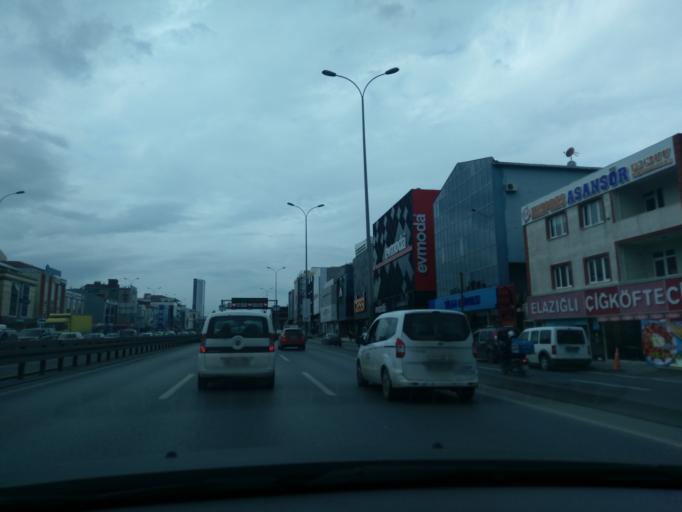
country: TR
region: Istanbul
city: Yakuplu
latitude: 40.9886
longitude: 28.7174
